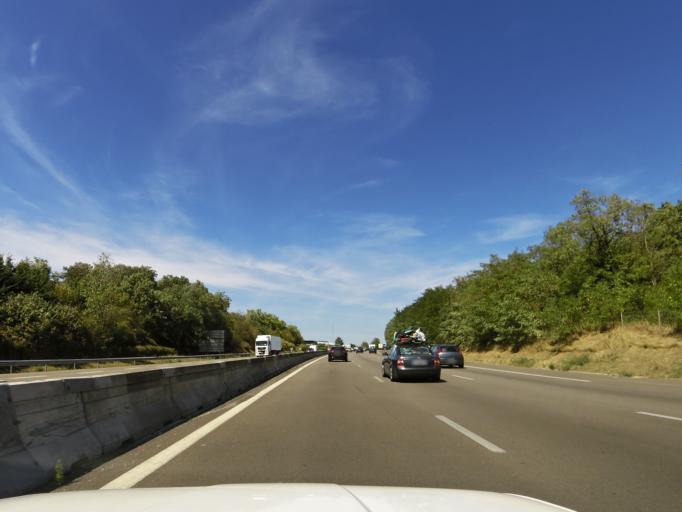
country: FR
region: Rhone-Alpes
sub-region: Departement de l'Isere
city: Roussillon
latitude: 45.3869
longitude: 4.8056
